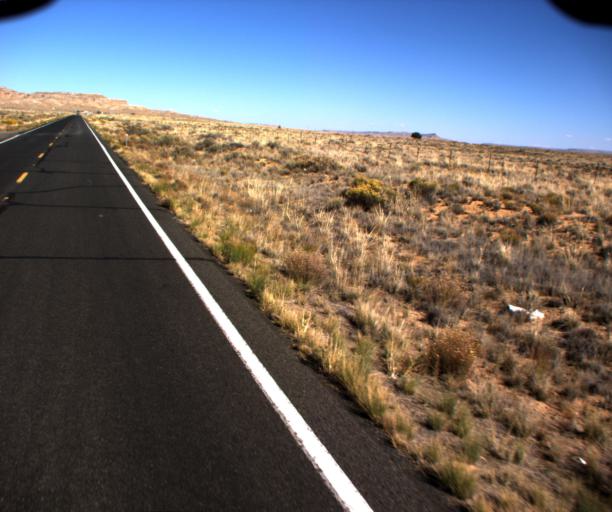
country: US
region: Arizona
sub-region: Navajo County
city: First Mesa
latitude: 35.7619
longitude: -110.5101
